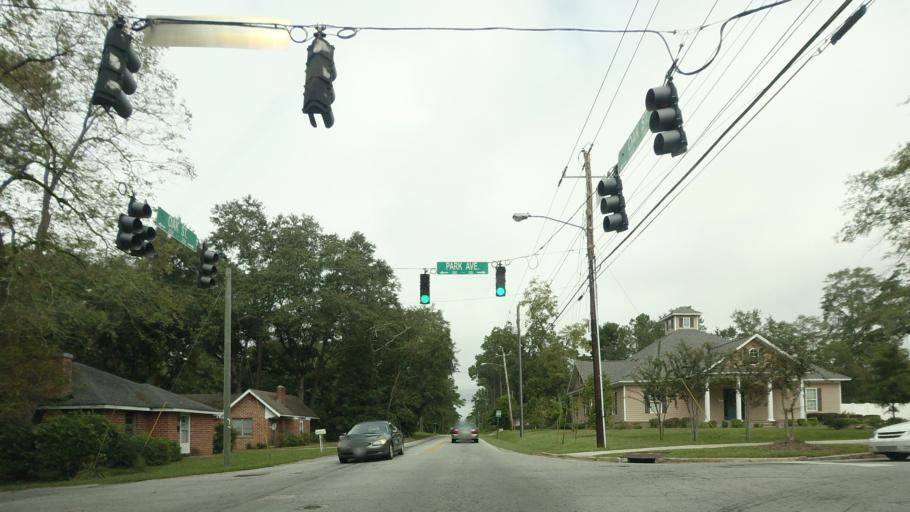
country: US
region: Georgia
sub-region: Lowndes County
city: Remerton
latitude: 30.8566
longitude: -83.2926
